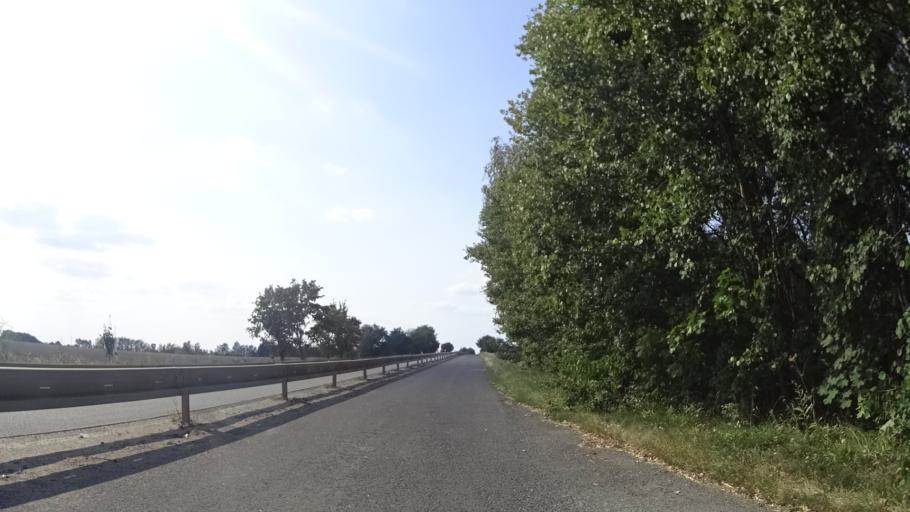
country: CZ
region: Kralovehradecky
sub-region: Okres Jicin
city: Sobotka
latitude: 50.4608
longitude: 15.2087
